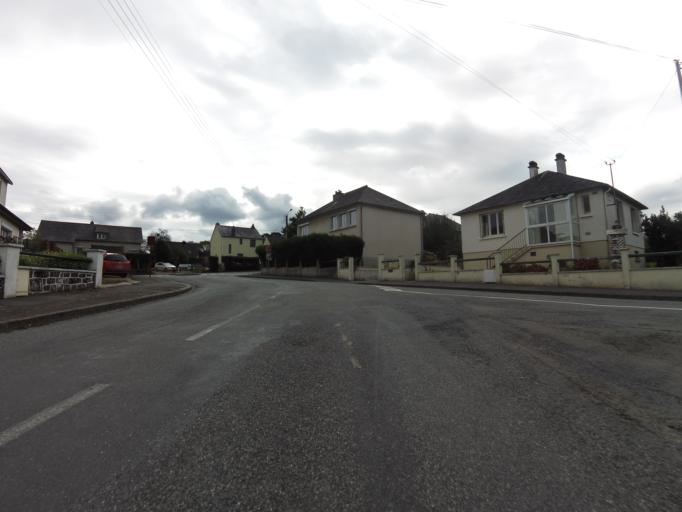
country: FR
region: Brittany
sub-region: Departement d'Ille-et-Vilaine
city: Montfort-sur-Meu
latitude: 48.1334
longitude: -1.9591
